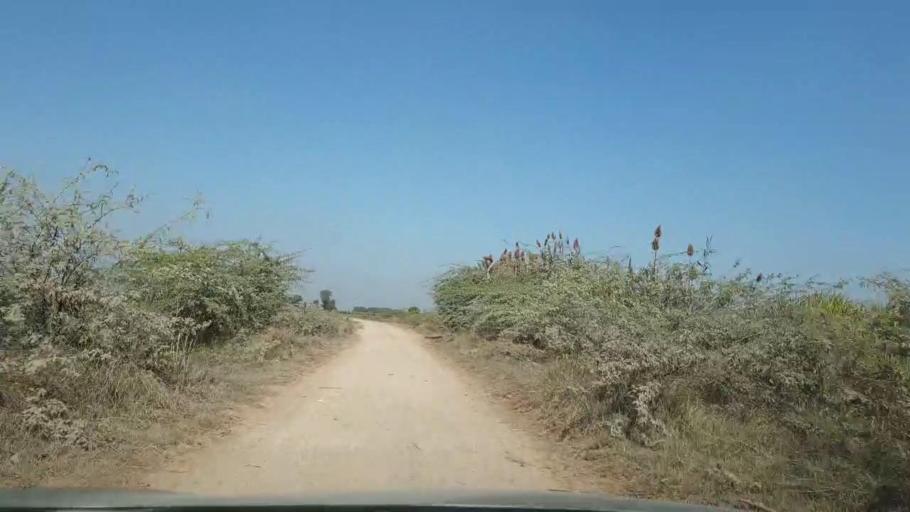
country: PK
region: Sindh
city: Tando Adam
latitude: 25.6336
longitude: 68.6676
